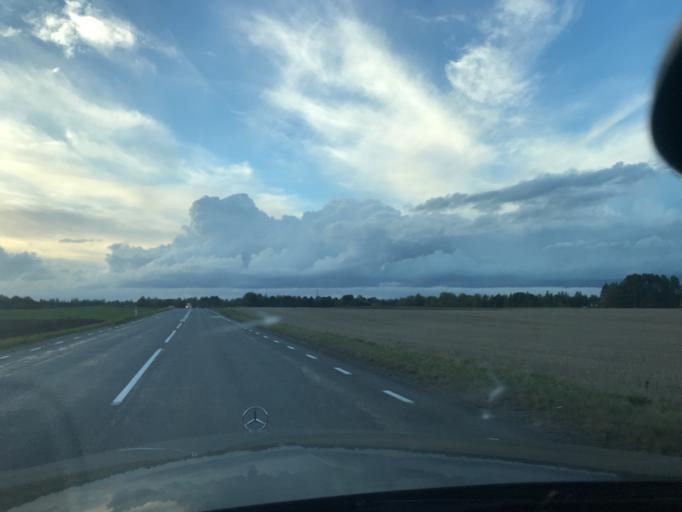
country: EE
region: Vorumaa
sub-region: Antsla vald
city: Vana-Antsla
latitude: 57.8878
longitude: 26.5148
